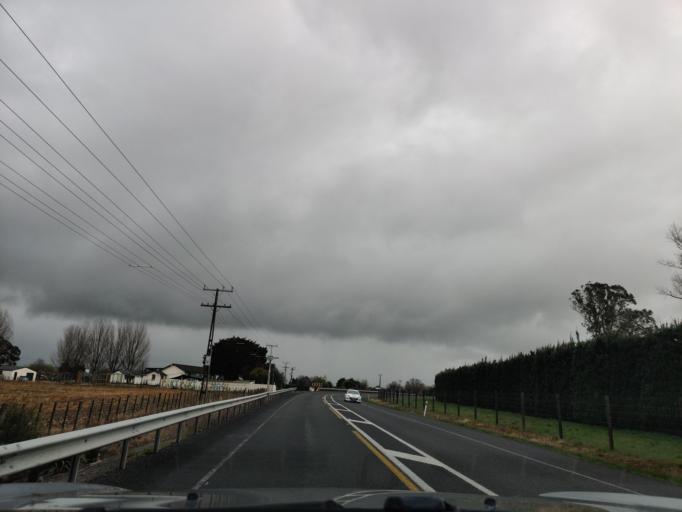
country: NZ
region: Hawke's Bay
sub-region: Hastings District
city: Hastings
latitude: -39.6885
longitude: 176.7888
